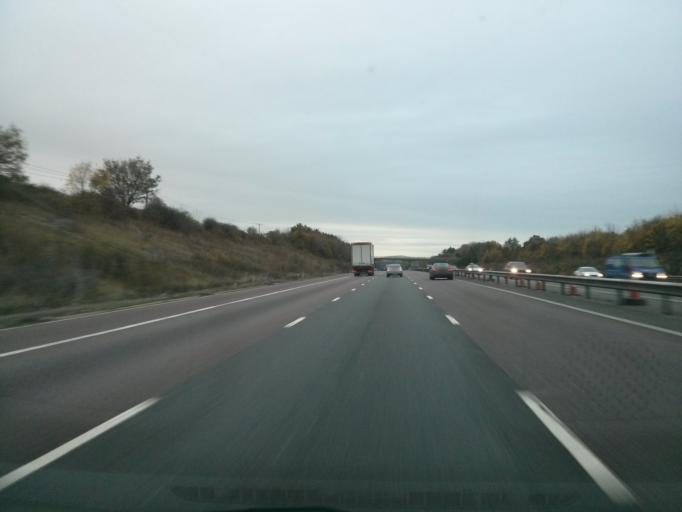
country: GB
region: England
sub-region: Gloucestershire
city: Churchdown
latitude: 51.8662
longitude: -2.1615
